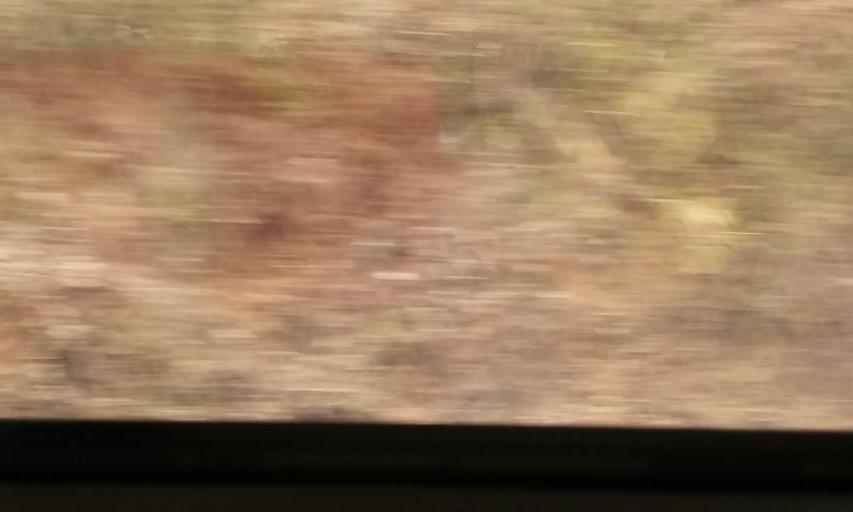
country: JP
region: Nagano
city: Ina
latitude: 35.7753
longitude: 137.6938
